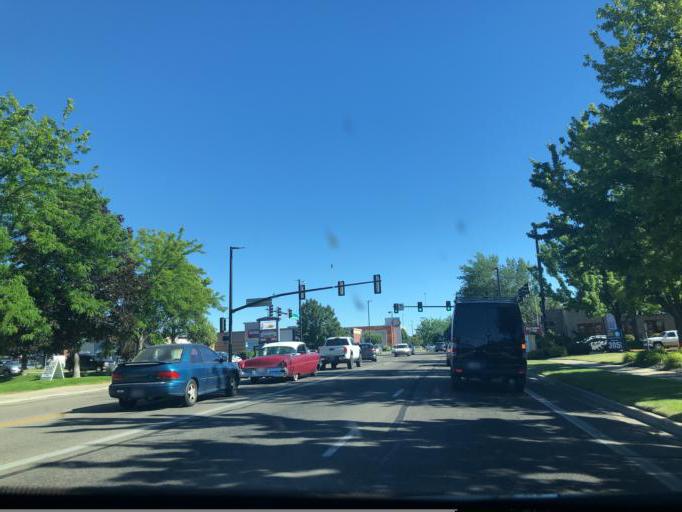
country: US
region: Idaho
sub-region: Ada County
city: Garden City
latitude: 43.6119
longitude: -116.2842
